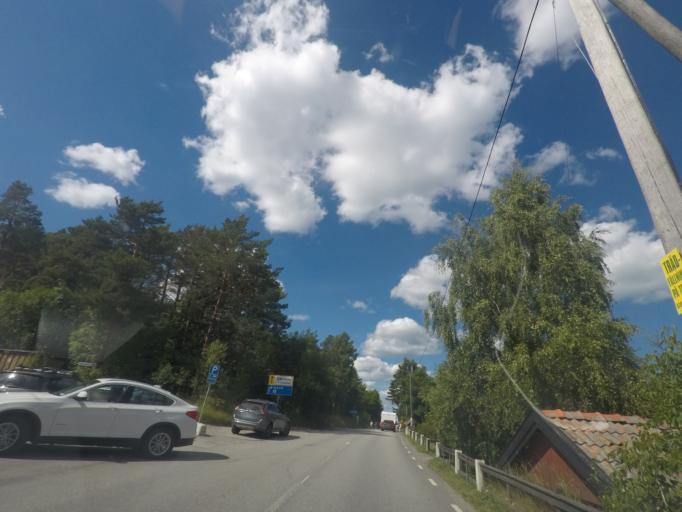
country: SE
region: Stockholm
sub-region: Norrtalje Kommun
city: Arno
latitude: 60.1007
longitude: 18.8072
